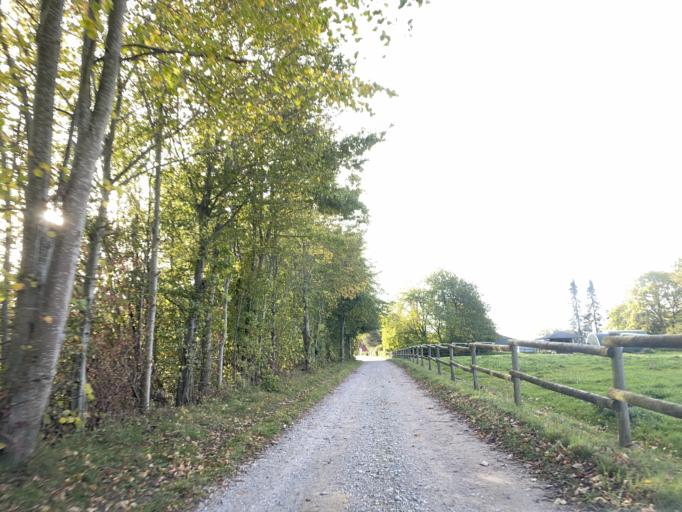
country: DK
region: Capital Region
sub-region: Allerod Kommune
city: Lynge
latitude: 55.8179
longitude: 12.2834
